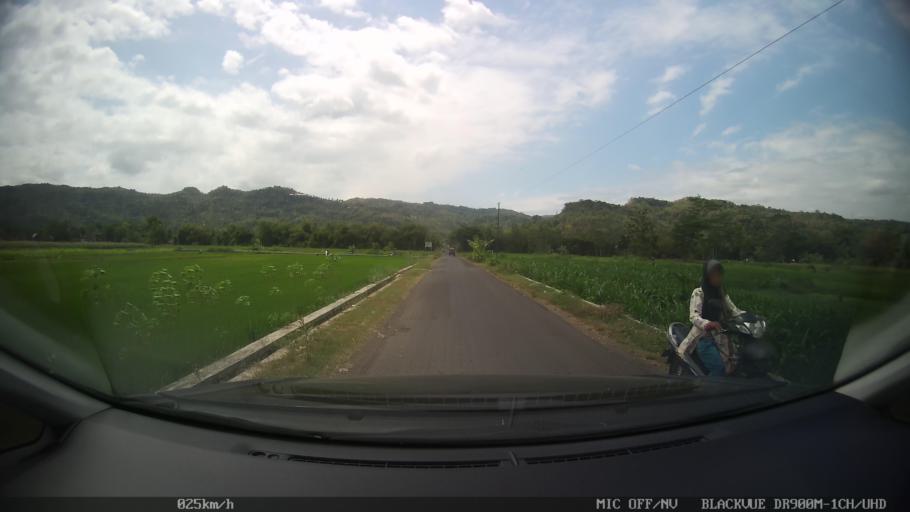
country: ID
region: Central Java
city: Candi Prambanan
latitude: -7.8110
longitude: 110.5010
